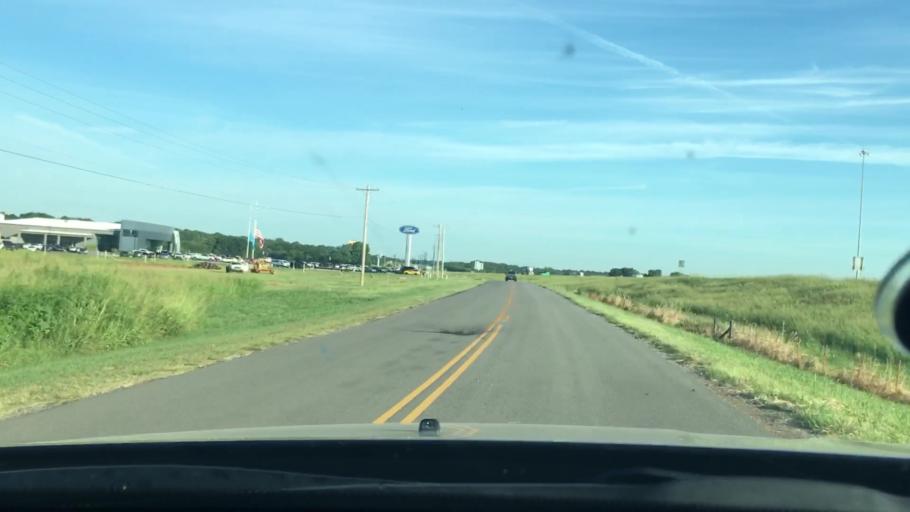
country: US
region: Oklahoma
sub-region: Garvin County
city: Pauls Valley
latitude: 34.7409
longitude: -97.2657
